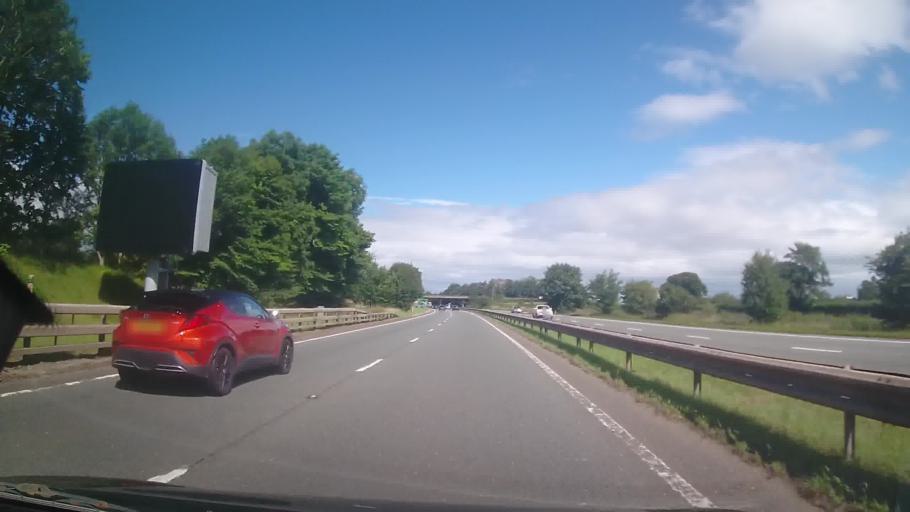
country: GB
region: Wales
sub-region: County of Flintshire
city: Flint
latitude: 53.2043
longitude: -3.1179
